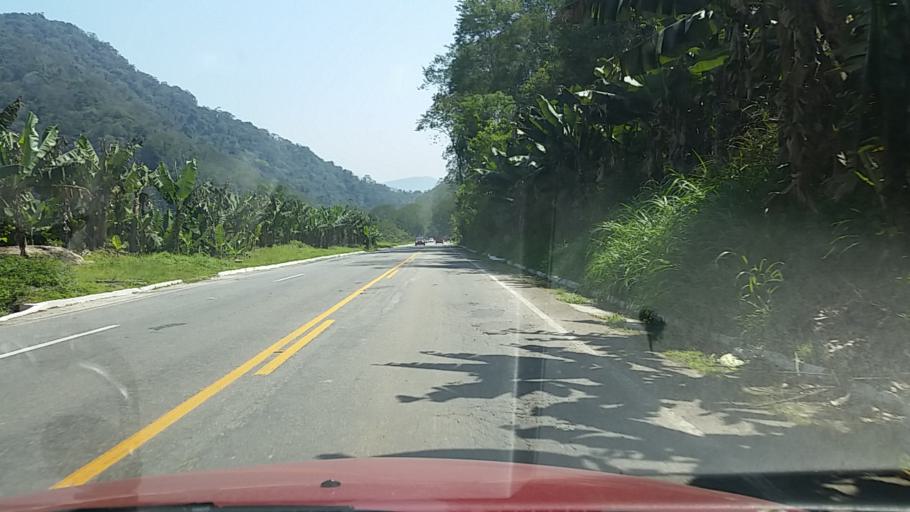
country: BR
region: Sao Paulo
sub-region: Miracatu
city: Miracatu
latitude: -24.3395
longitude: -47.4997
